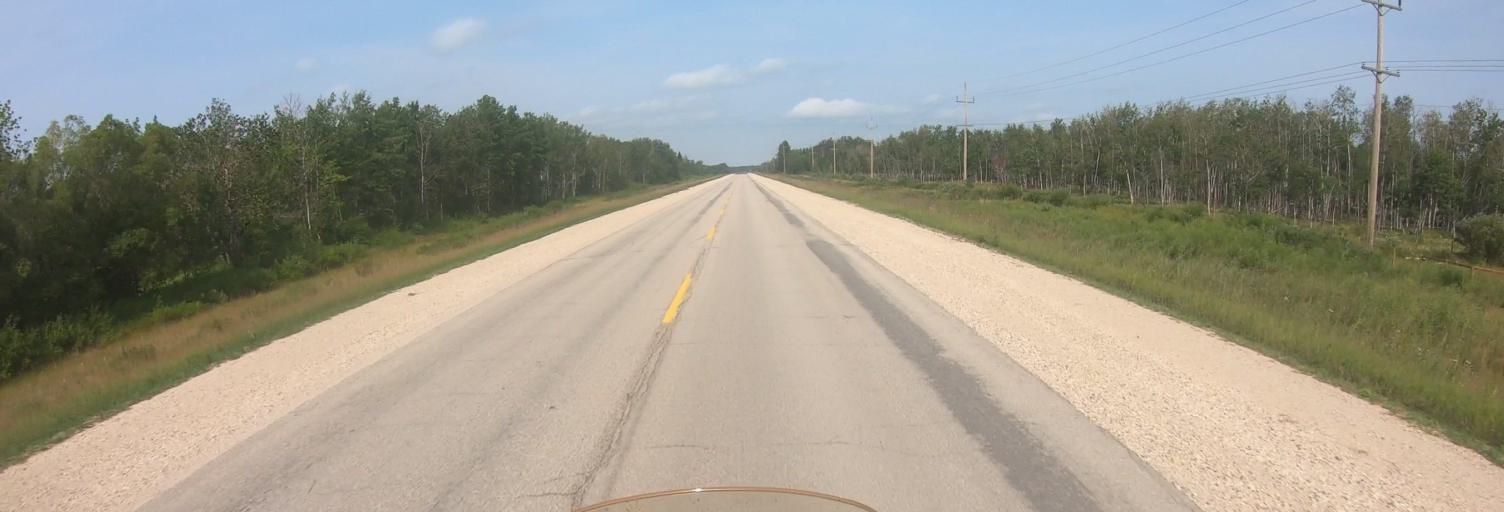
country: CA
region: Manitoba
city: Steinbach
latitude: 49.3623
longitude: -96.6736
